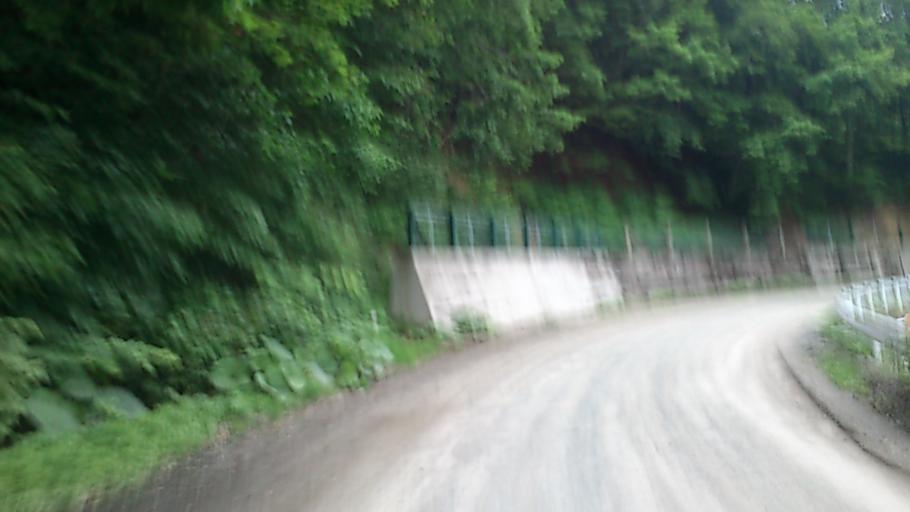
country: JP
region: Aomori
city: Hirosaki
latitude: 40.5376
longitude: 140.1834
